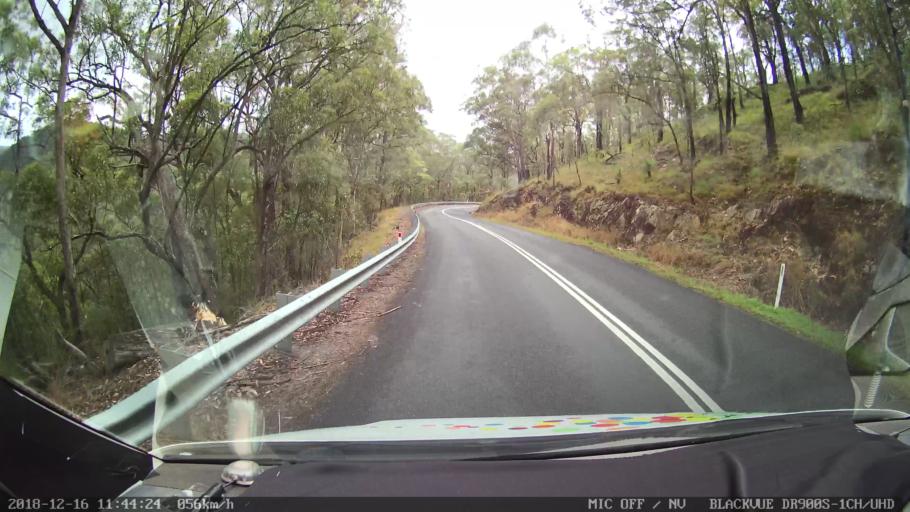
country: AU
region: New South Wales
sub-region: Tenterfield Municipality
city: Carrolls Creek
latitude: -28.9385
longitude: 152.2197
